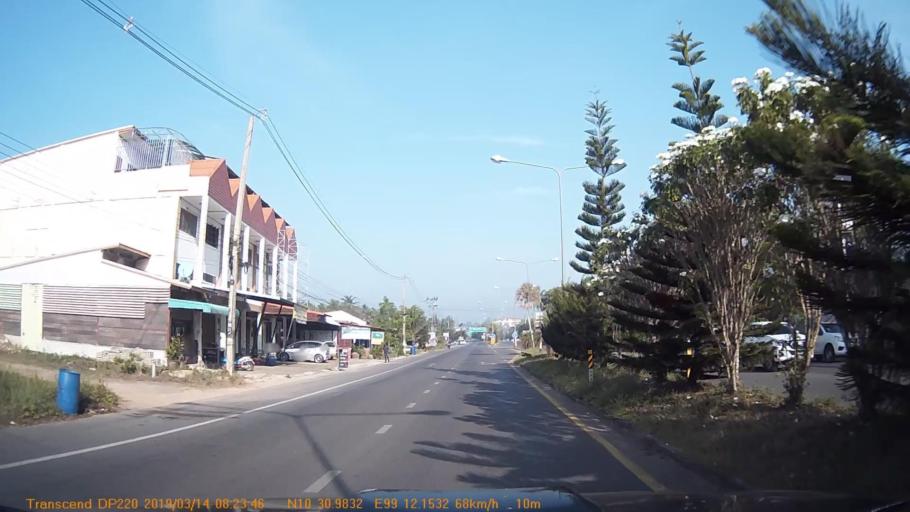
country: TH
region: Chumphon
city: Chumphon
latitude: 10.5165
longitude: 99.2024
